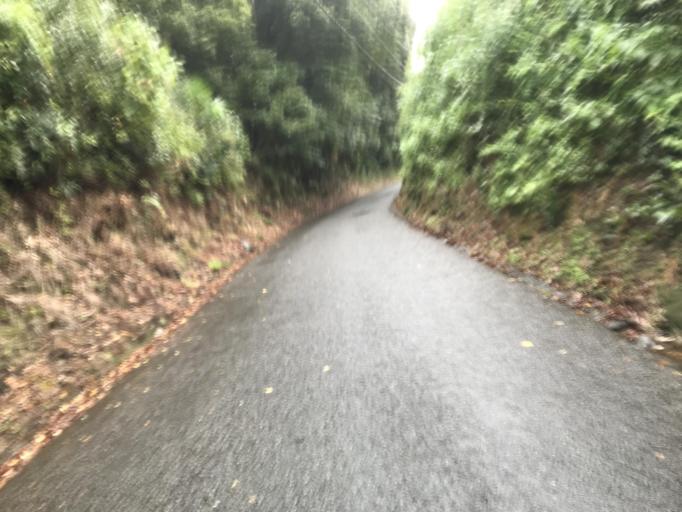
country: JP
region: Kanagawa
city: Zama
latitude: 35.5502
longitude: 139.3256
